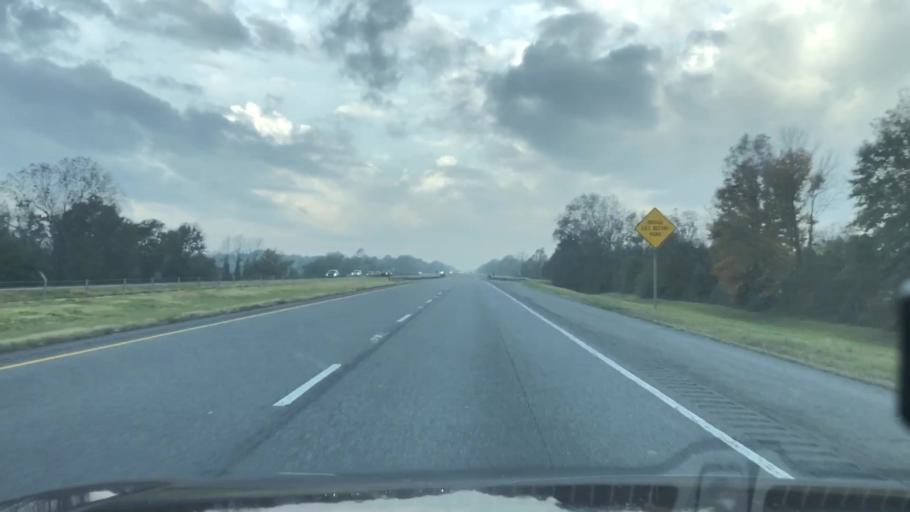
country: US
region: Louisiana
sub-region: Madison Parish
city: Tallulah
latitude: 32.4063
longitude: -91.2322
